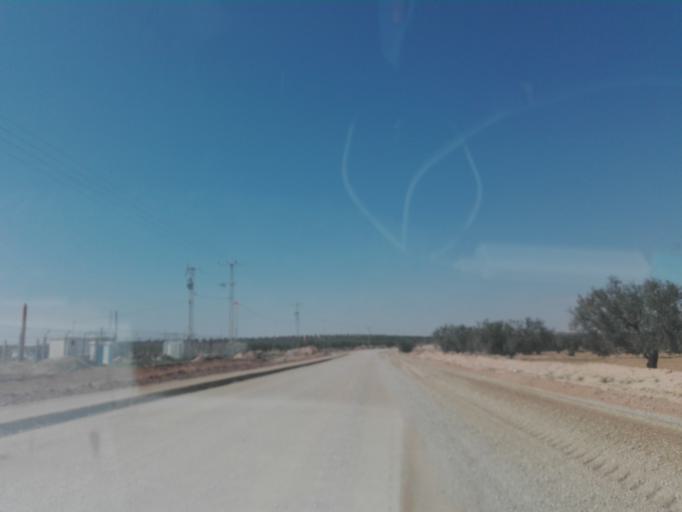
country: TN
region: Safaqis
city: Sfax
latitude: 34.6770
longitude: 10.4499
